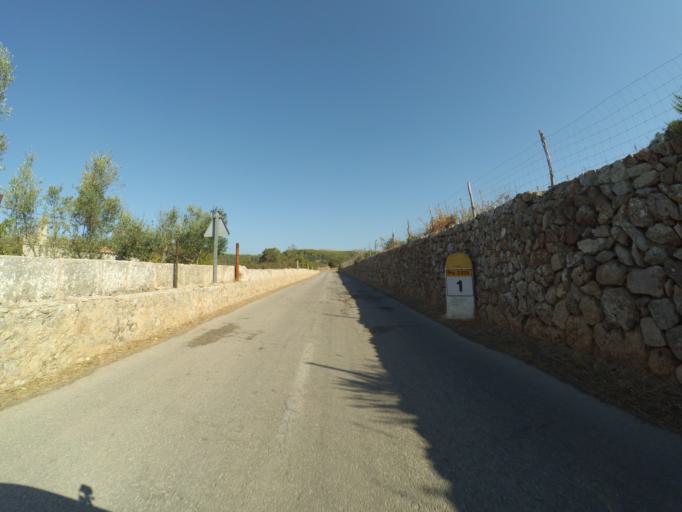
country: ES
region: Balearic Islands
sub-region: Illes Balears
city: Arta
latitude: 39.7046
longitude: 3.3512
